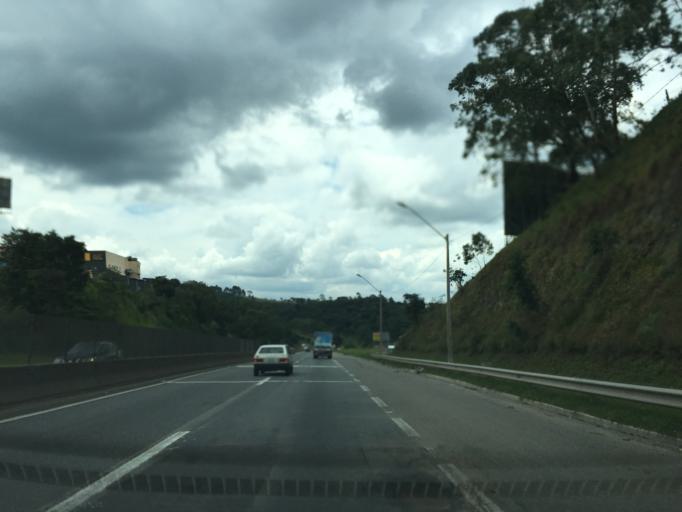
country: BR
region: Sao Paulo
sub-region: Mairipora
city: Mairipora
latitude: -23.2573
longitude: -46.5913
